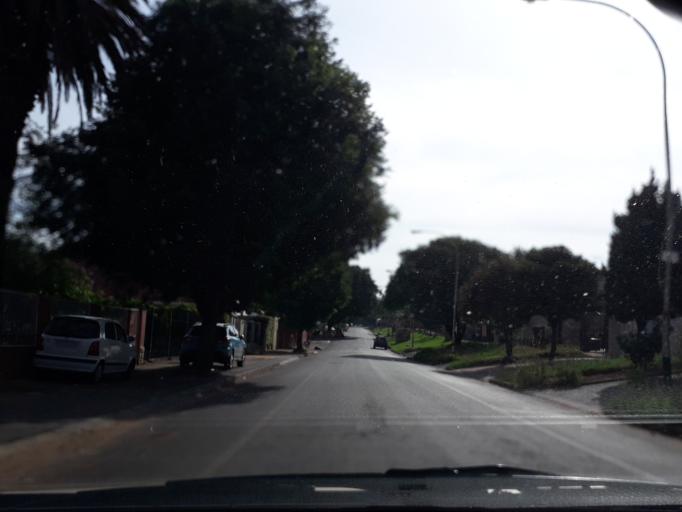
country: ZA
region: Gauteng
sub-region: City of Johannesburg Metropolitan Municipality
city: Johannesburg
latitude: -26.1875
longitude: 28.0765
